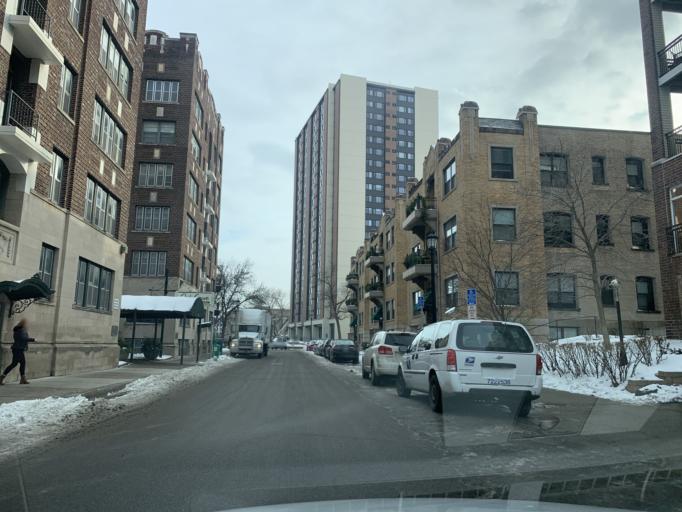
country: US
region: Minnesota
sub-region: Hennepin County
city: Minneapolis
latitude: 44.9668
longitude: -93.2828
